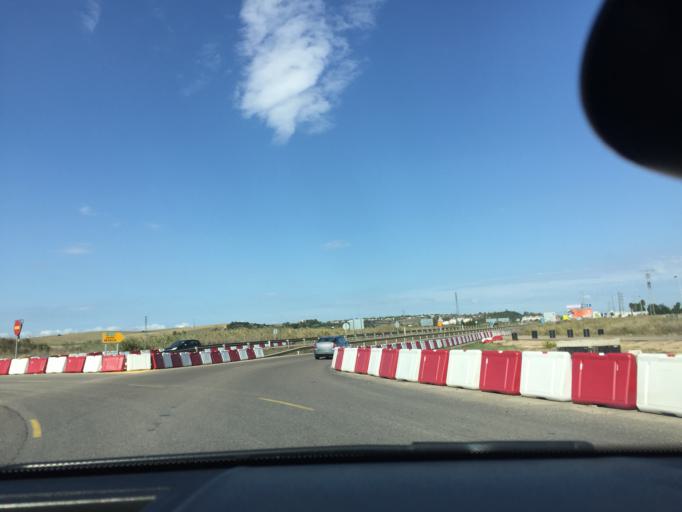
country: ES
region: Andalusia
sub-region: Provincia de Sevilla
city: Palomares del Rio
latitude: 37.3077
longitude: -6.0387
